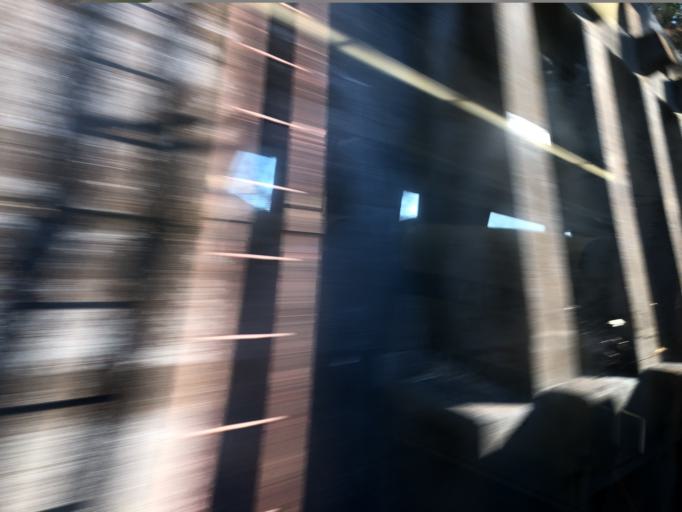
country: JP
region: Kochi
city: Nakamura
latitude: 33.0121
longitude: 132.9905
